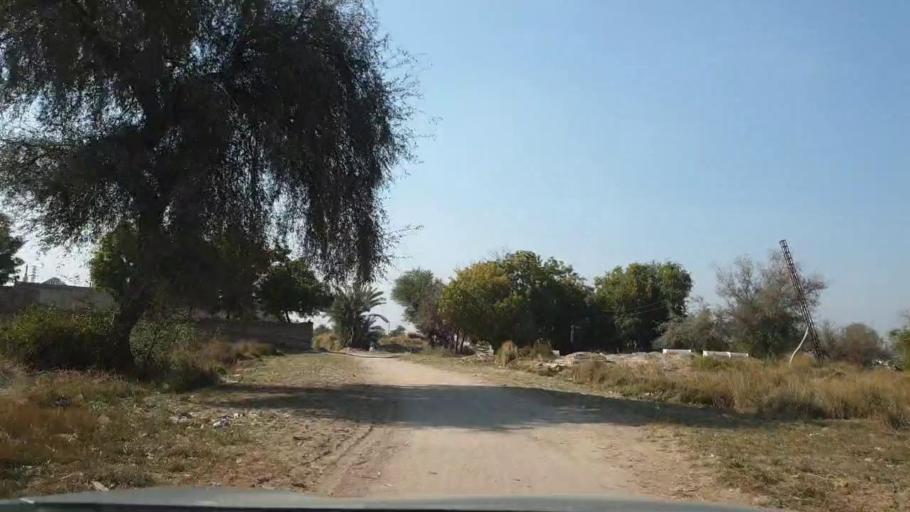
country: PK
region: Sindh
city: Berani
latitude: 25.6868
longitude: 68.7763
